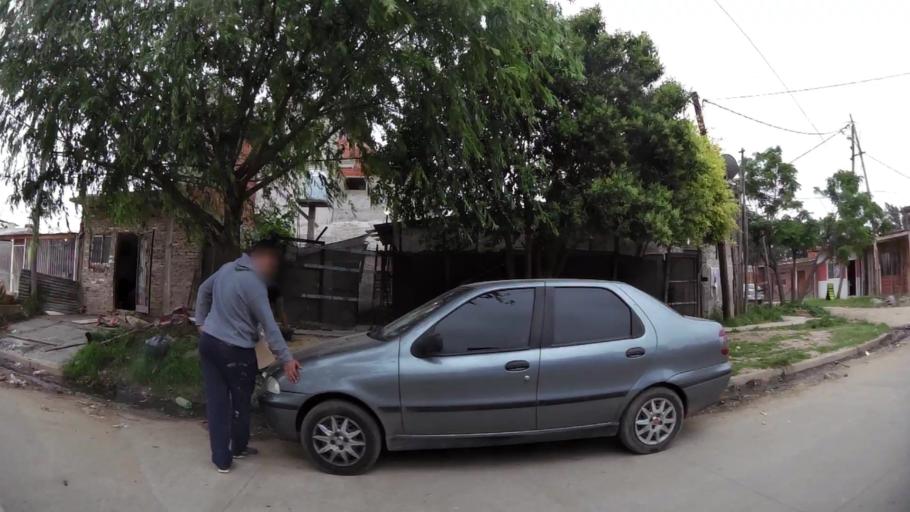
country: AR
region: Buenos Aires
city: San Justo
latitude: -34.6993
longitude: -58.5493
